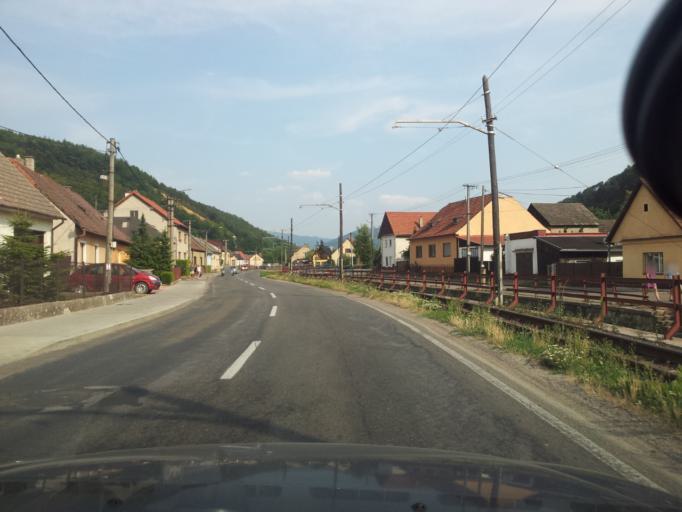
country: SK
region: Trenciansky
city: Nova Dubnica
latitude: 48.9336
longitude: 18.1221
